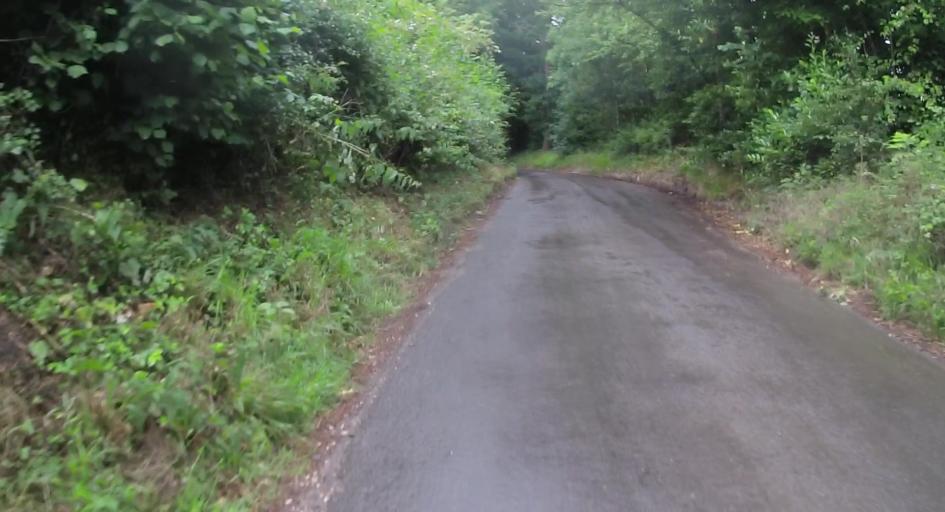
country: GB
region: England
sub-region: Hampshire
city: Long Sutton
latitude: 51.1708
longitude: -0.9205
